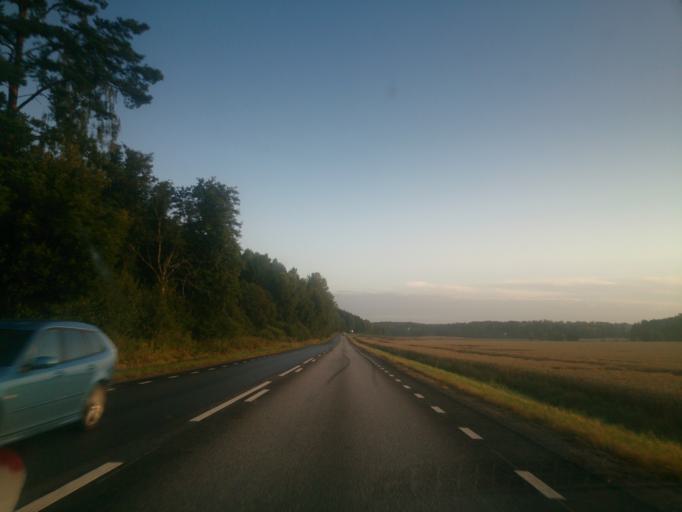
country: SE
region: Soedermanland
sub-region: Nykopings Kommun
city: Nykoping
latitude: 58.8049
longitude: 17.0820
